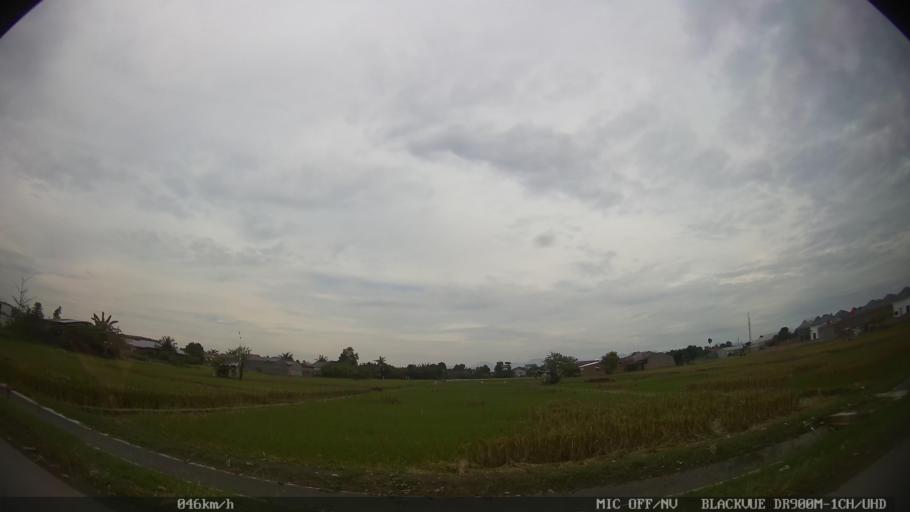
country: ID
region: North Sumatra
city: Sunggal
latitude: 3.6141
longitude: 98.5971
